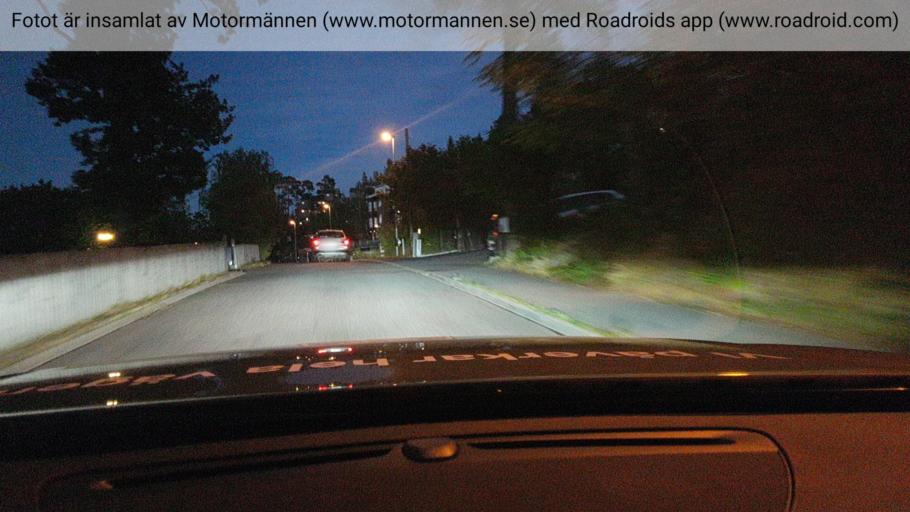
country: SE
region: Stockholm
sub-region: Nacka Kommun
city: Fisksatra
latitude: 59.2524
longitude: 18.2781
